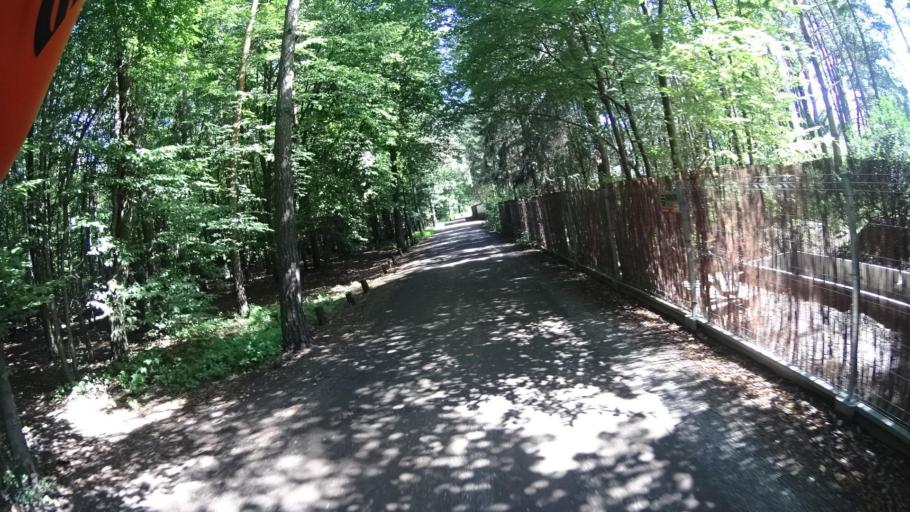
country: PL
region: Masovian Voivodeship
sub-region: Powiat piaseczynski
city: Jozefoslaw
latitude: 52.1086
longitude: 21.0565
